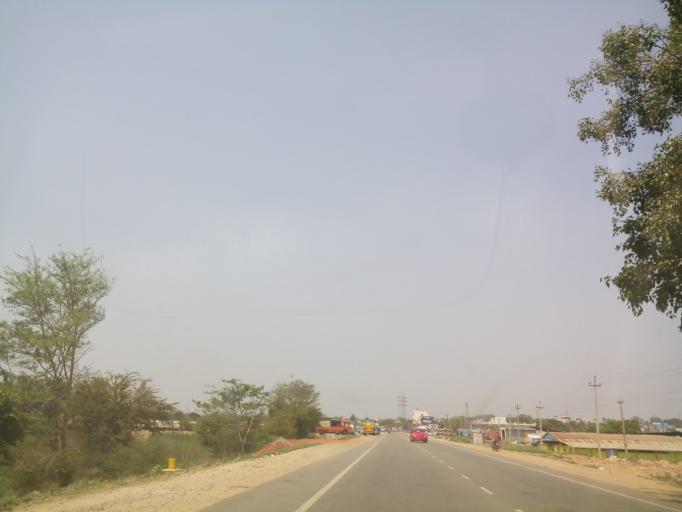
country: IN
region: Karnataka
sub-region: Hassan
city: Hassan
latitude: 12.9909
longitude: 76.0898
